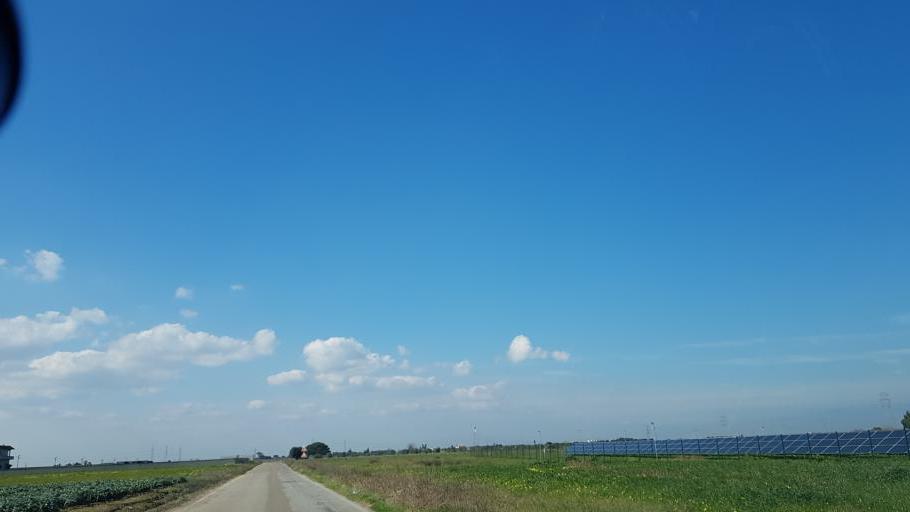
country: IT
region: Apulia
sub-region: Provincia di Brindisi
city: La Rosa
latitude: 40.5901
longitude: 17.9294
